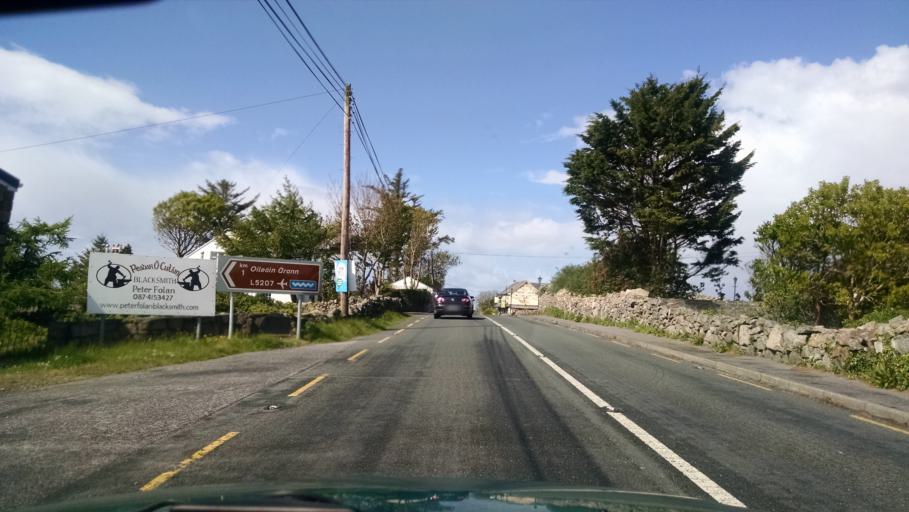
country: IE
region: Connaught
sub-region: County Galway
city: Oughterard
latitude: 53.2387
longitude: -9.4767
